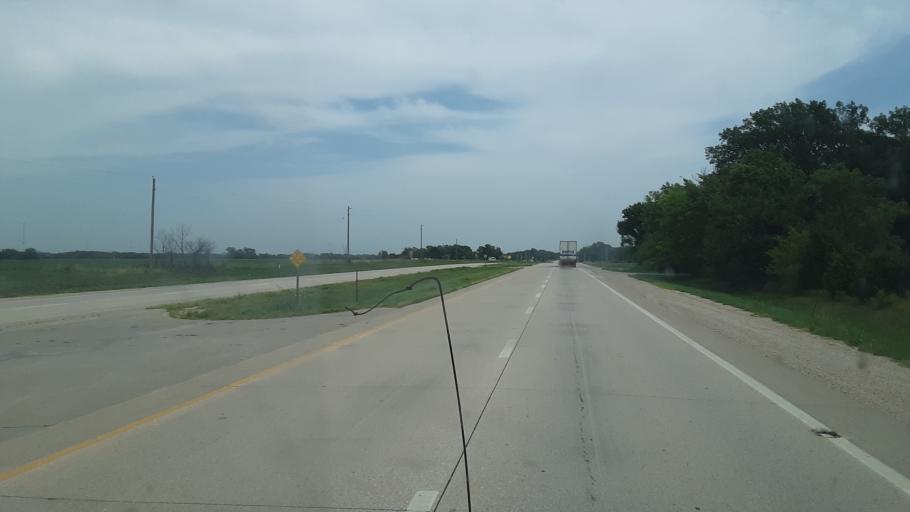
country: US
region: Kansas
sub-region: Allen County
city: Iola
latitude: 37.9220
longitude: -95.3250
